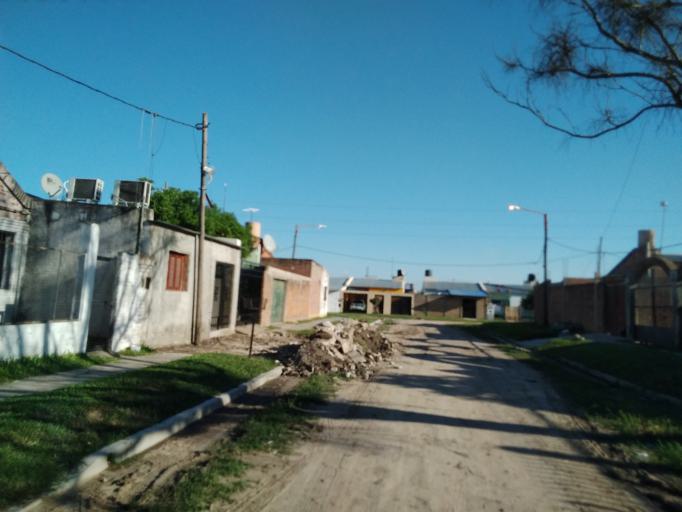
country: AR
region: Corrientes
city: Corrientes
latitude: -27.5074
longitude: -58.7797
